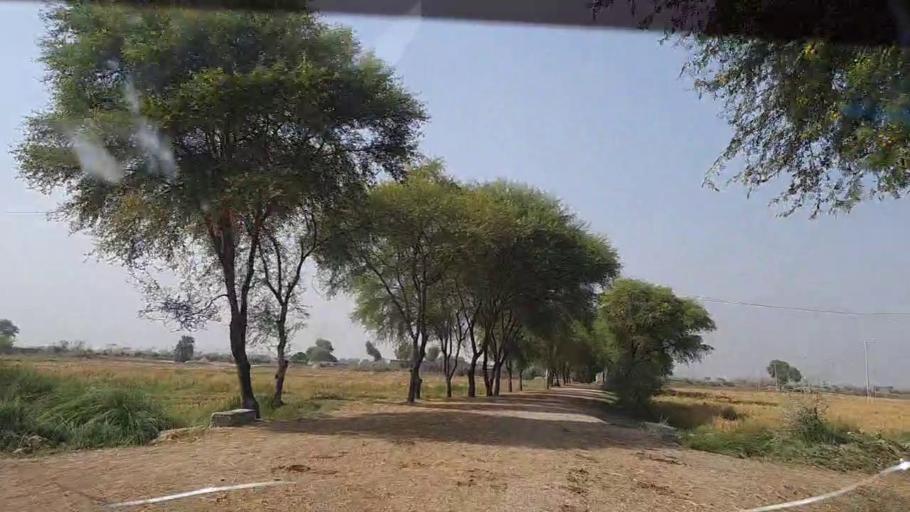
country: PK
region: Sindh
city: Shikarpur
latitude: 28.1154
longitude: 68.6575
